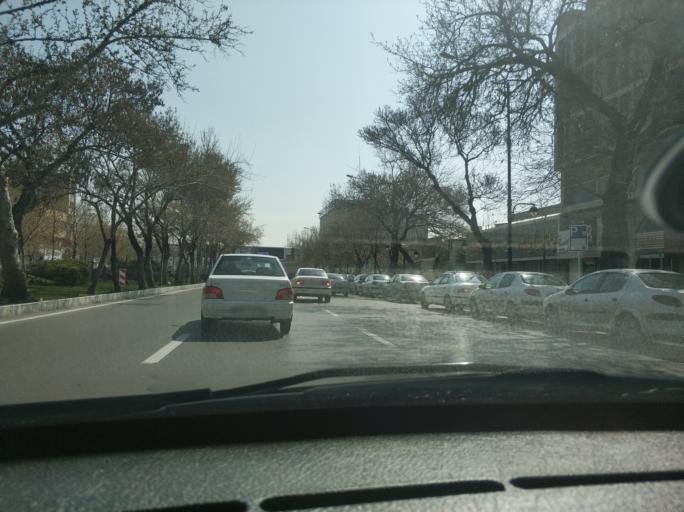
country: IR
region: Razavi Khorasan
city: Mashhad
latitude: 36.2979
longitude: 59.5700
